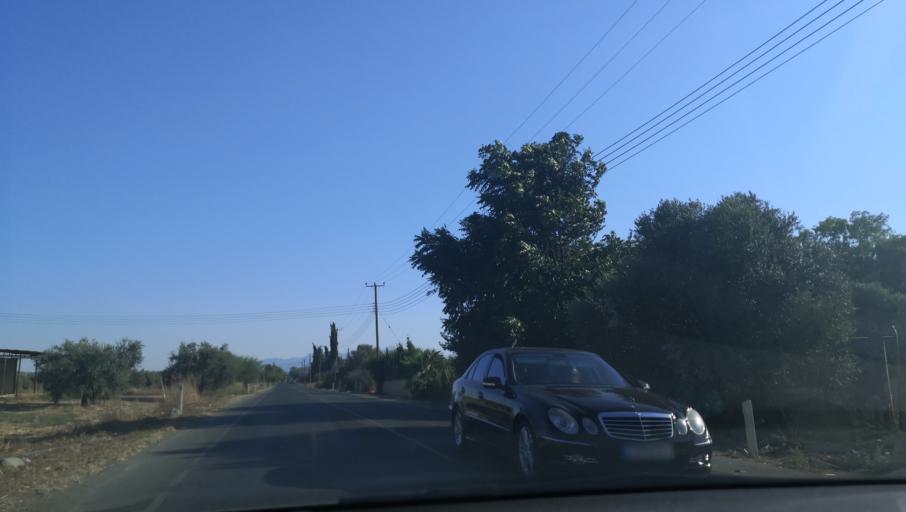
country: CY
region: Lefkosia
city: Pano Deftera
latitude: 35.0693
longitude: 33.2680
